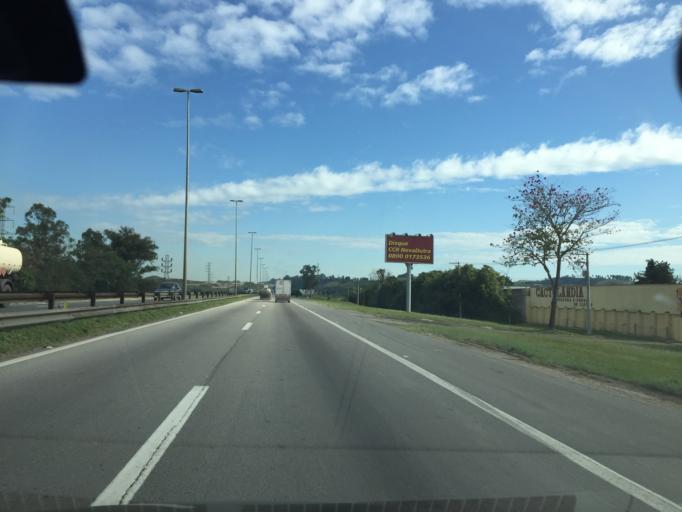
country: BR
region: Sao Paulo
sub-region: Jacarei
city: Jacarei
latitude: -23.2856
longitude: -45.9908
